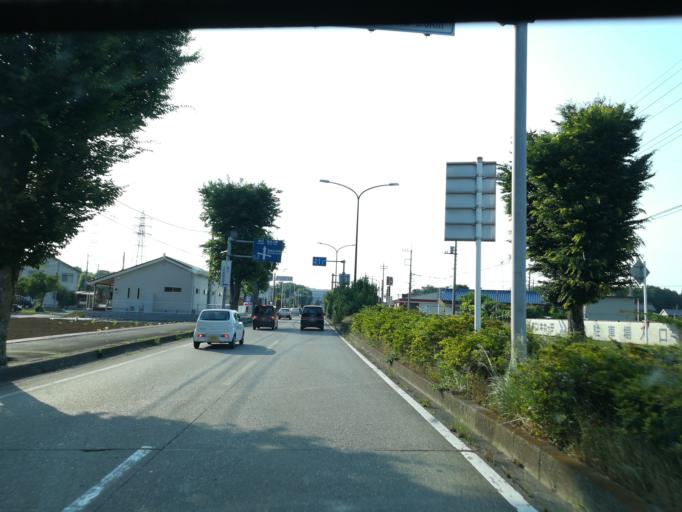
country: JP
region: Saitama
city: Sakado
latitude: 36.0362
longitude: 139.3835
